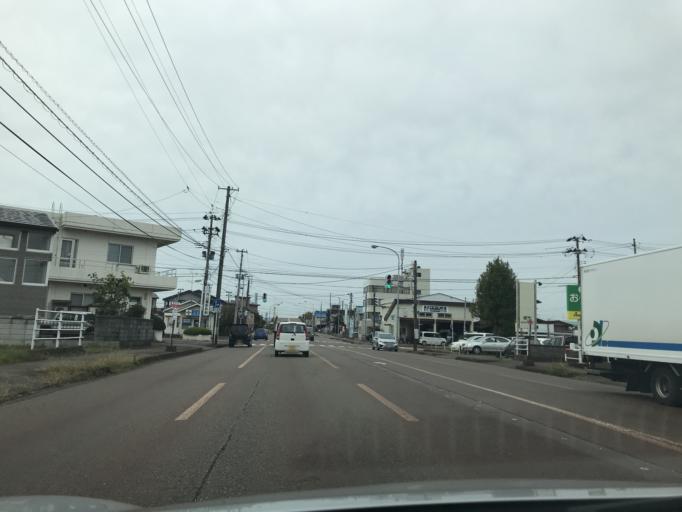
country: JP
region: Niigata
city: Nagaoka
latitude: 37.4244
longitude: 138.8465
